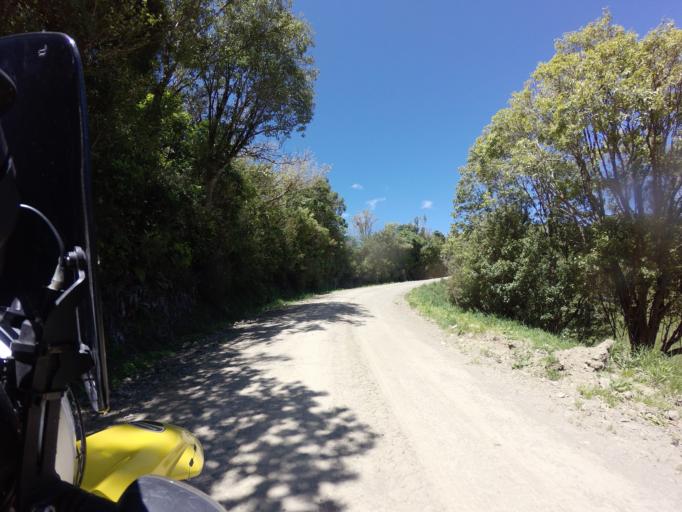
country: NZ
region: Bay of Plenty
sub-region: Opotiki District
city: Opotiki
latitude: -38.4076
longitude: 177.4443
